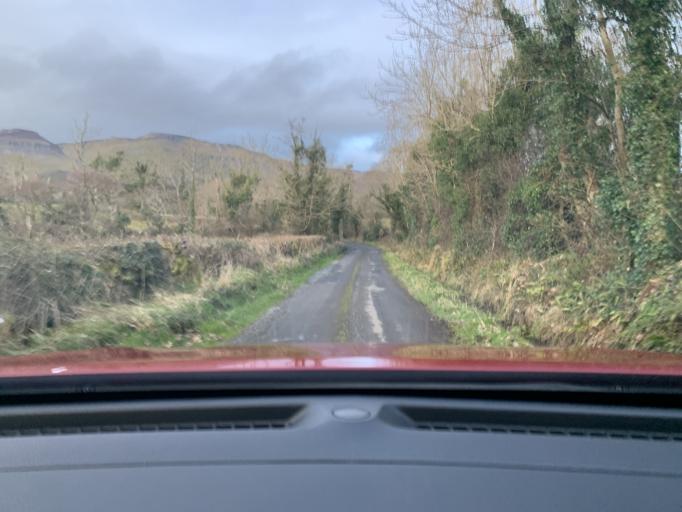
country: IE
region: Connaught
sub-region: Sligo
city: Sligo
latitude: 54.3159
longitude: -8.4483
